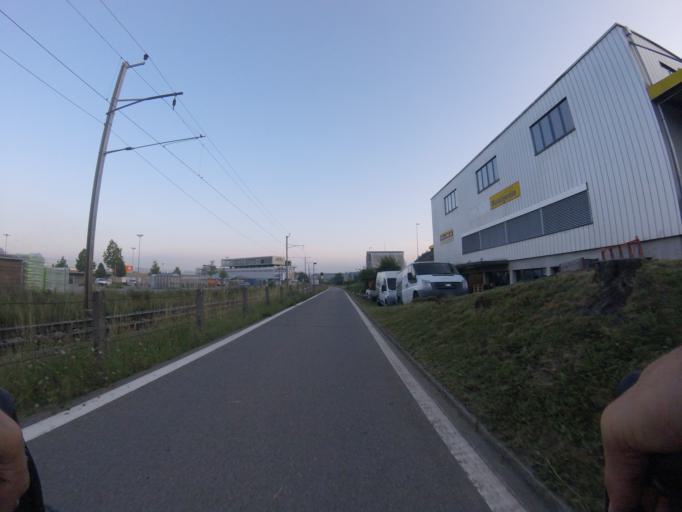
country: CH
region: Bern
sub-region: Thun District
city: Heimberg
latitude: 46.7793
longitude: 7.6113
